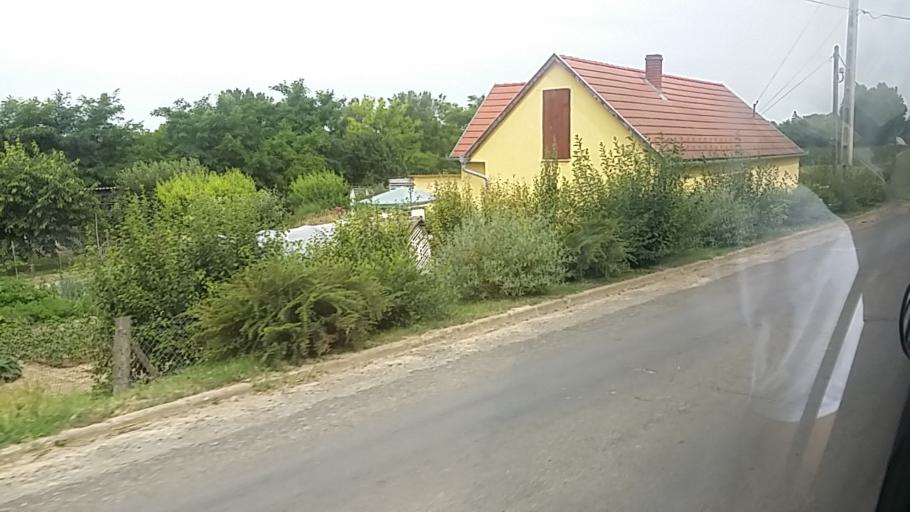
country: HU
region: Baranya
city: Boly
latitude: 45.9307
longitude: 18.4688
